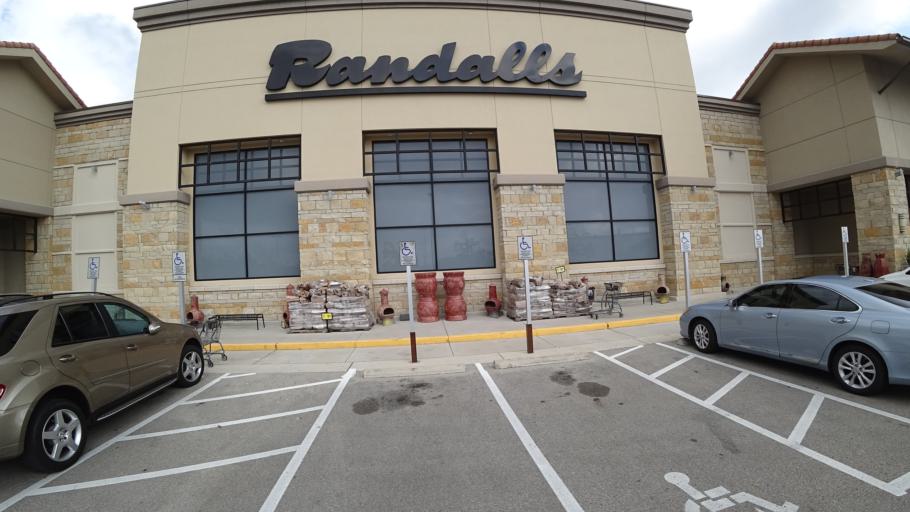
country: US
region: Texas
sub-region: Travis County
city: Hudson Bend
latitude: 30.3889
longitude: -97.8842
